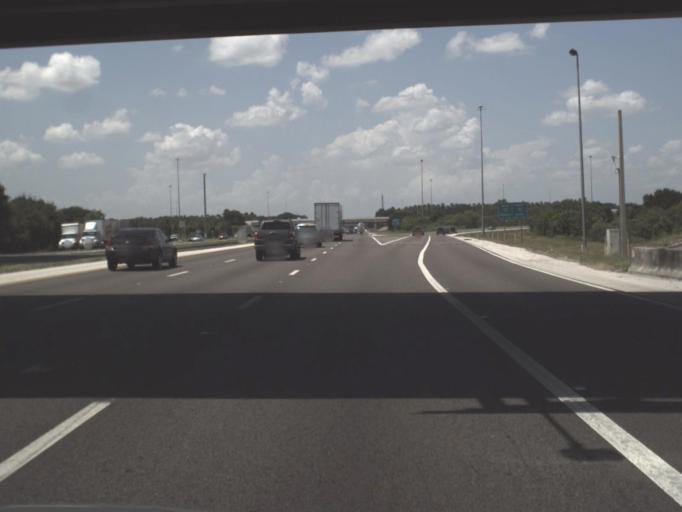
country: US
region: Florida
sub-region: Hillsborough County
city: Mango
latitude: 28.0034
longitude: -82.3189
